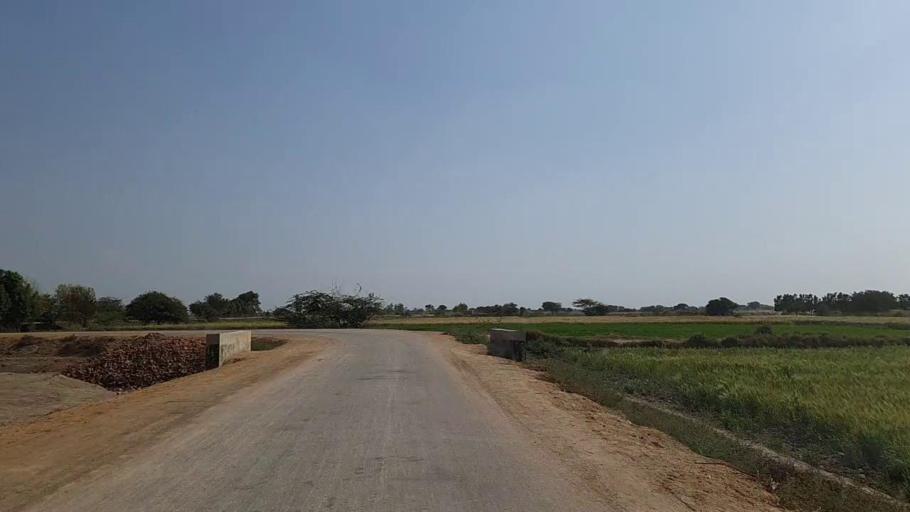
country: PK
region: Sindh
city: Daro Mehar
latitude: 24.7877
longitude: 68.1796
